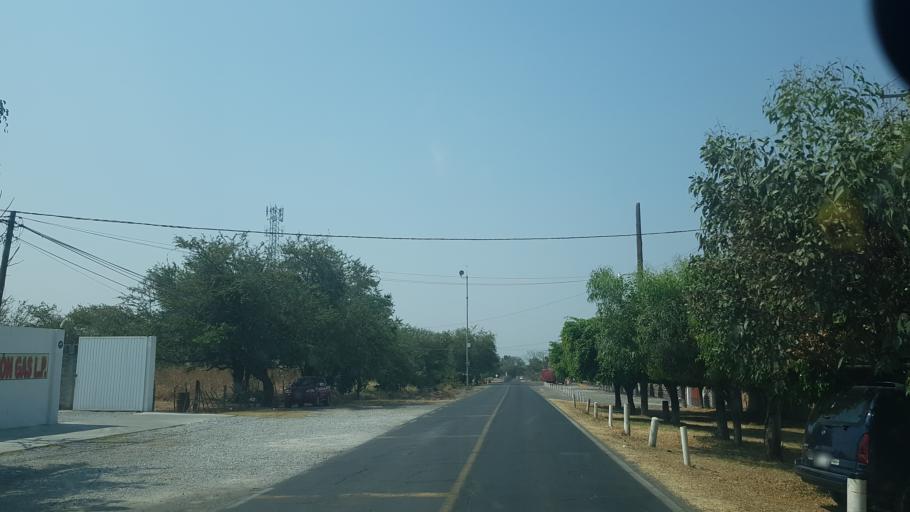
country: MX
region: Morelos
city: Amayuca
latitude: 18.7274
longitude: -98.7904
